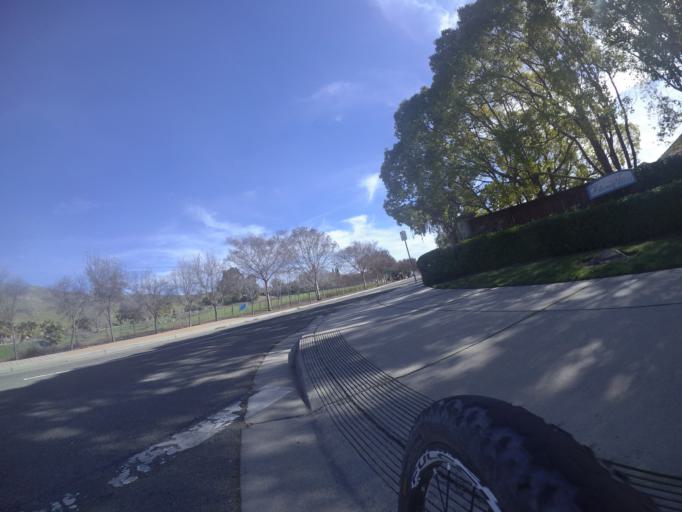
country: US
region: California
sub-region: Santa Clara County
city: Milpitas
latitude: 37.4229
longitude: -121.8619
